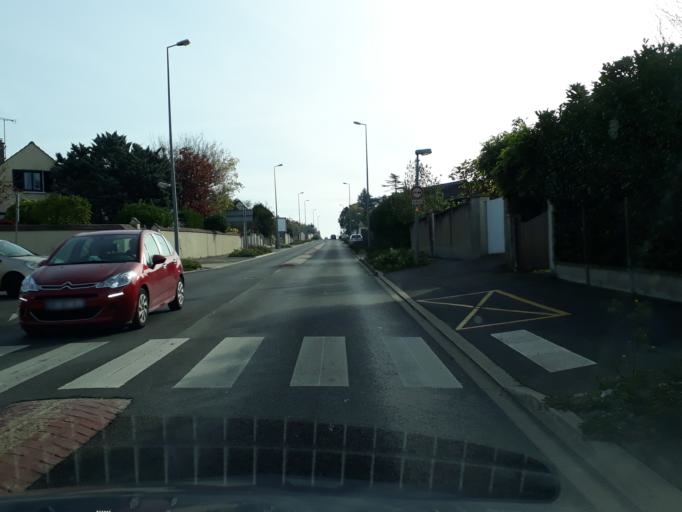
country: FR
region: Ile-de-France
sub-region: Departement de Seine-et-Marne
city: Samoreau
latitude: 48.4265
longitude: 2.7570
